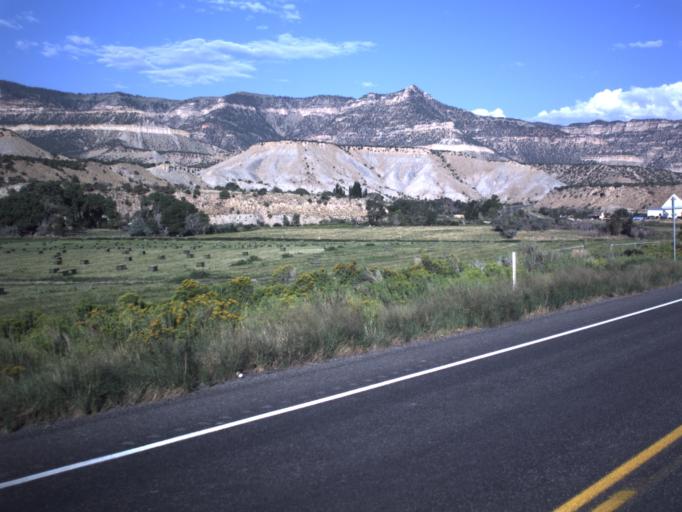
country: US
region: Utah
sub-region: Emery County
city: Huntington
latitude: 39.3615
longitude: -111.0341
